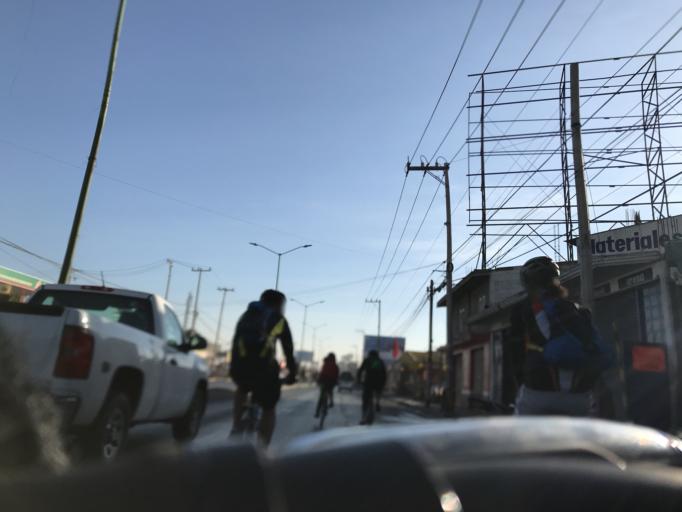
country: MX
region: Mexico
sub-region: Cuautitlan
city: La Trinidad
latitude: 19.6739
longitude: -99.1616
